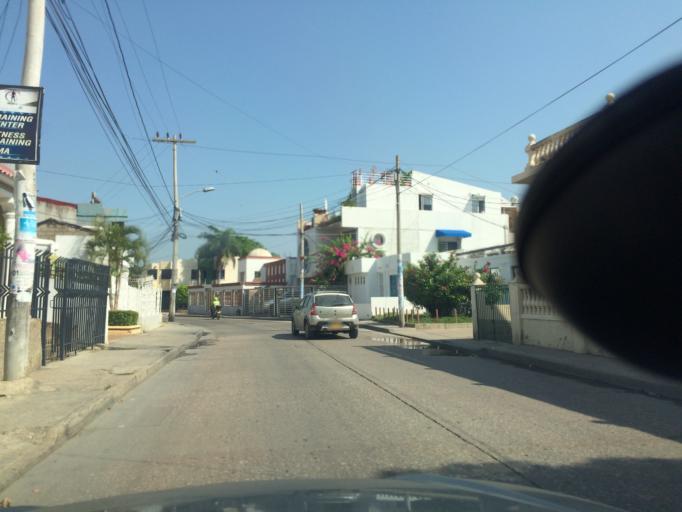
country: CO
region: Bolivar
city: Cartagena
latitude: 10.4164
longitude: -75.5361
